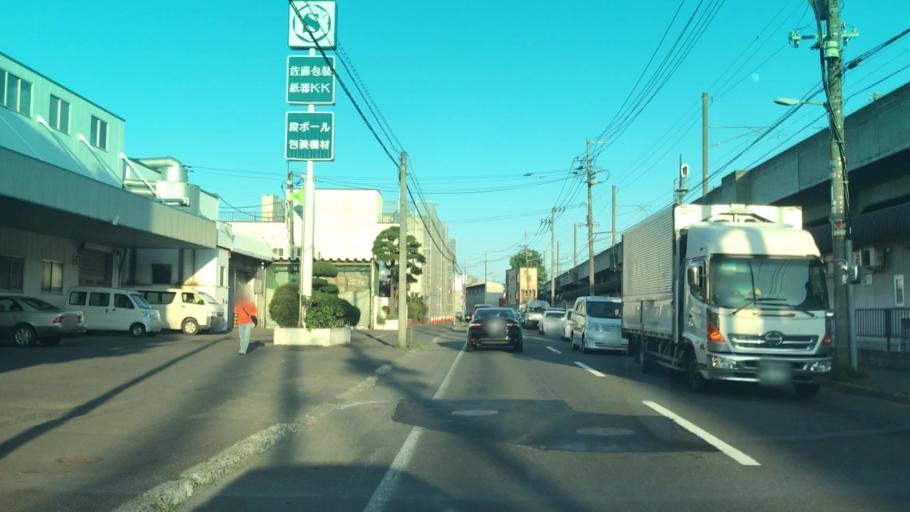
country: JP
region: Hokkaido
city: Sapporo
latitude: 43.0772
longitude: 141.3172
